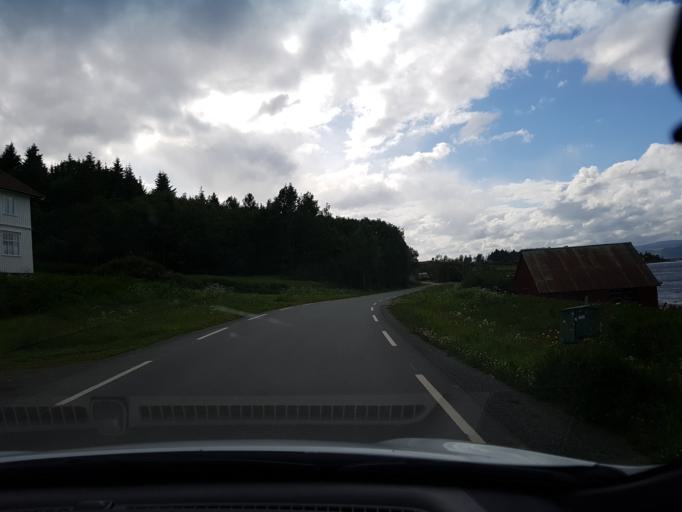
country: NO
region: Nord-Trondelag
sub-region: Frosta
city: Frosta
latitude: 63.6316
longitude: 10.7956
